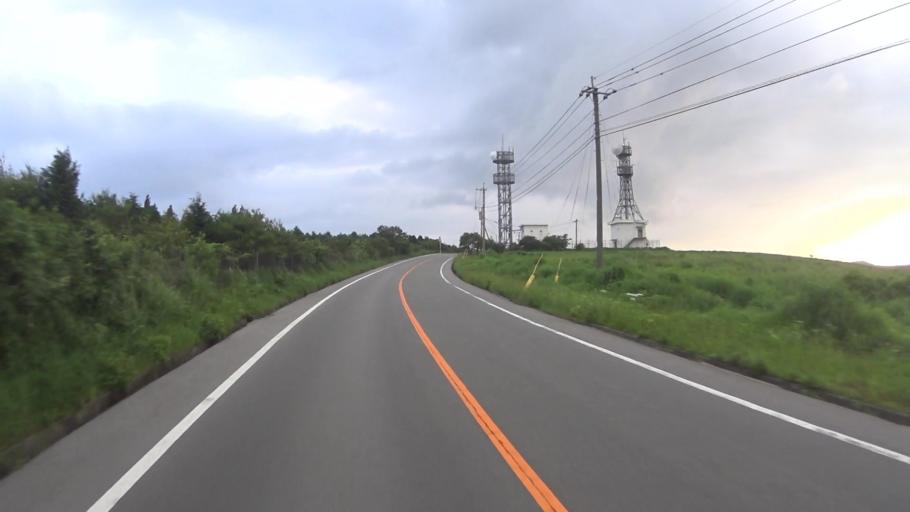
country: JP
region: Kumamoto
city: Aso
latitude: 32.9415
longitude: 130.9774
